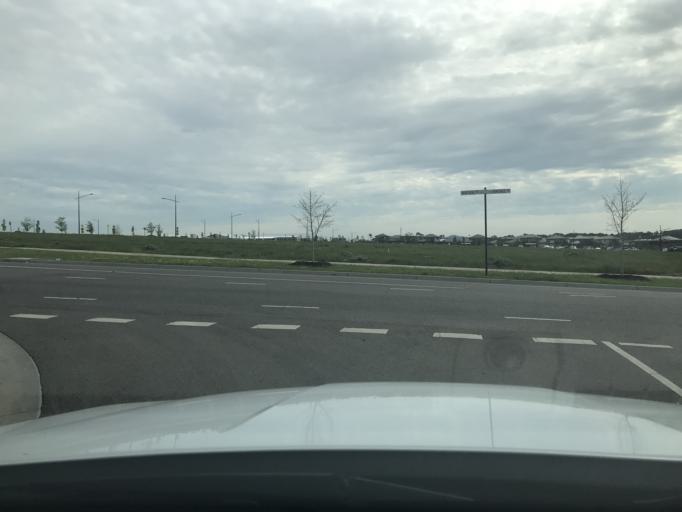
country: AU
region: Victoria
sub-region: Hume
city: Roxburgh Park
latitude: -37.5980
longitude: 144.8936
